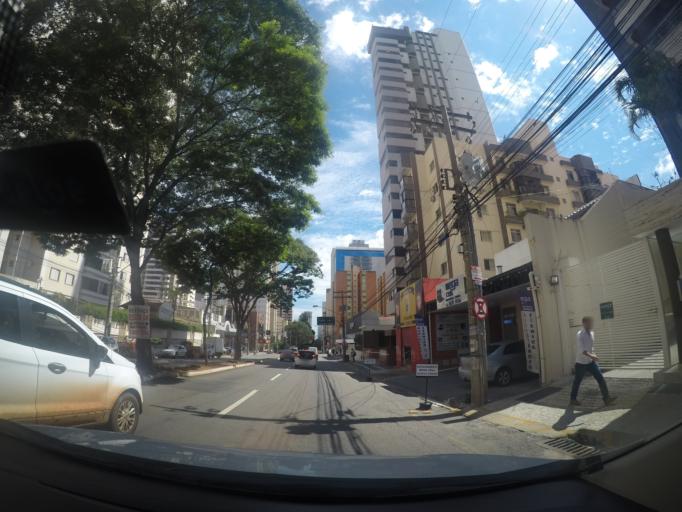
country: BR
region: Goias
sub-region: Goiania
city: Goiania
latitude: -16.7149
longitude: -49.2669
